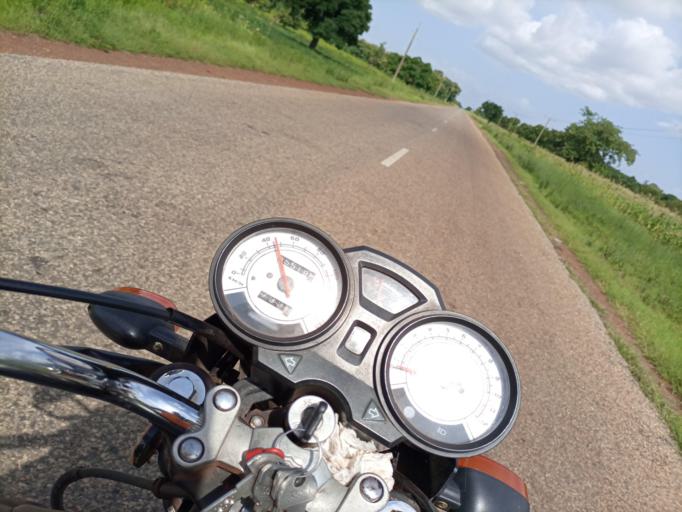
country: GH
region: Northern
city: Savelugu
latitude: 9.5735
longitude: -1.0068
